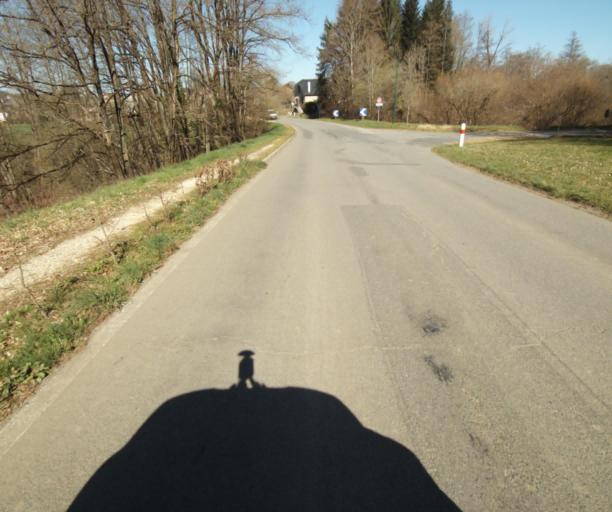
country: FR
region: Limousin
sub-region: Departement de la Correze
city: Seilhac
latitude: 45.3672
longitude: 1.7060
